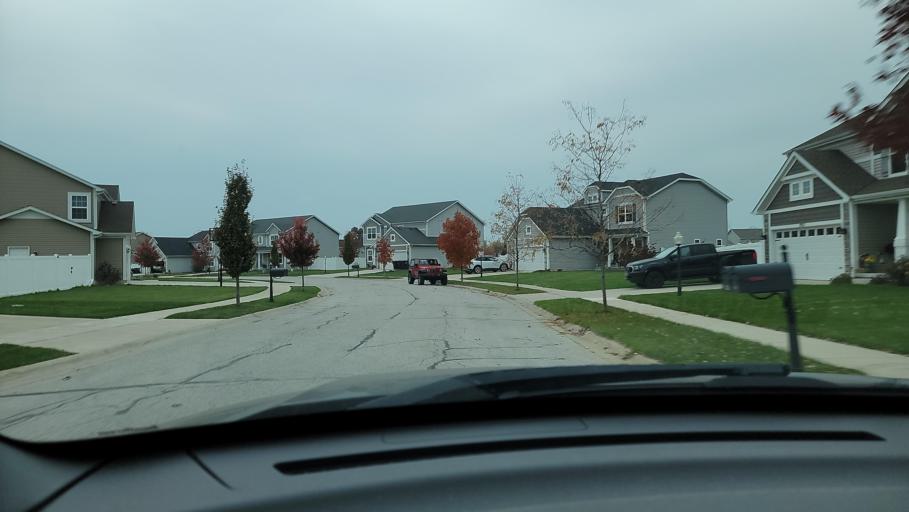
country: US
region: Indiana
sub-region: Porter County
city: Portage
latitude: 41.5665
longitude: -87.1662
